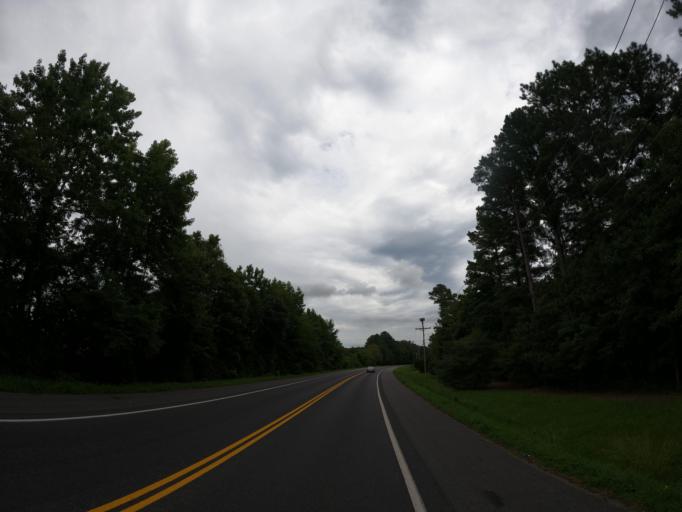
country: US
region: Maryland
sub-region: Saint Mary's County
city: Lexington Park
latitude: 38.1728
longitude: -76.5280
